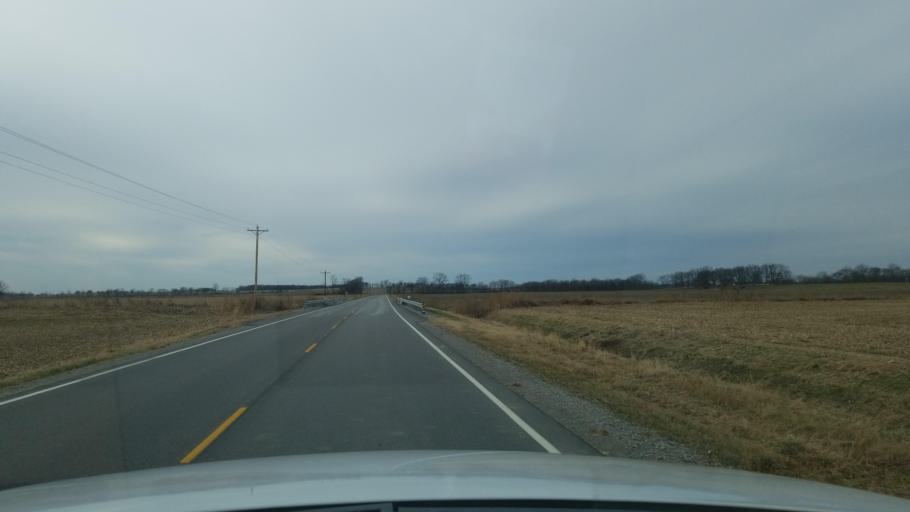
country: US
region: Illinois
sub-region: White County
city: Norris City
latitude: 37.9076
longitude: -88.1713
